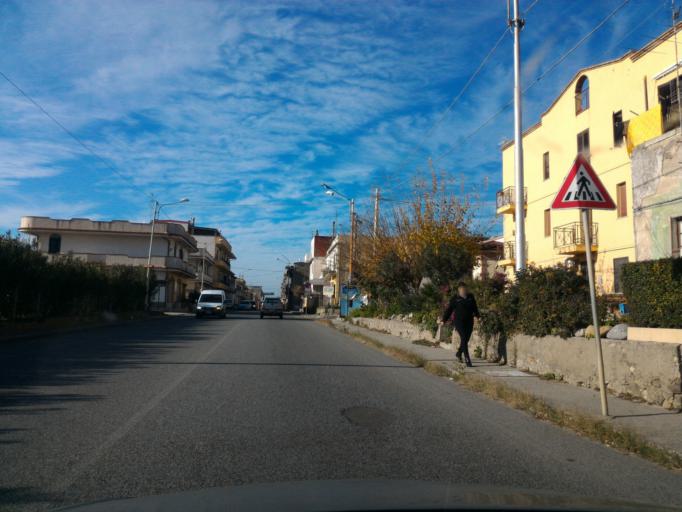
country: IT
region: Calabria
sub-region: Provincia di Catanzaro
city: Botricello
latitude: 38.9370
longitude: 16.8647
